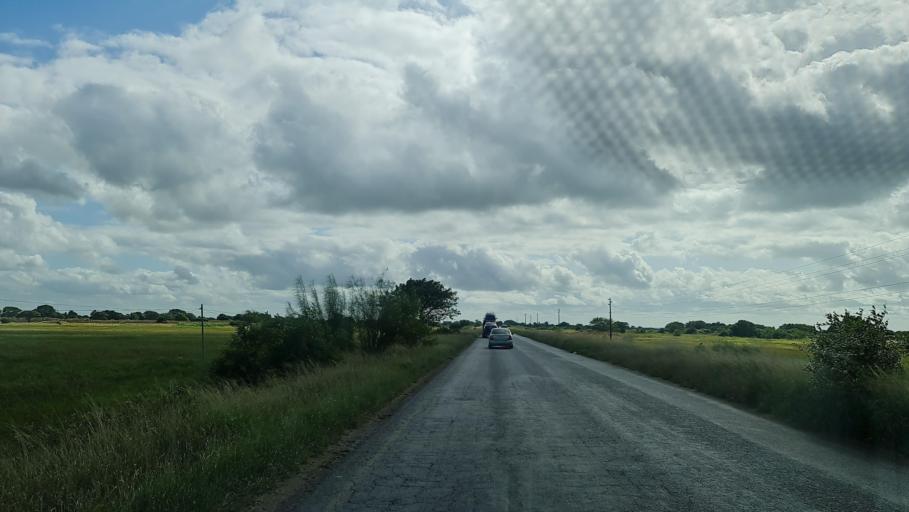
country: MZ
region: Gaza
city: Macia
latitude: -25.0932
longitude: 32.8357
